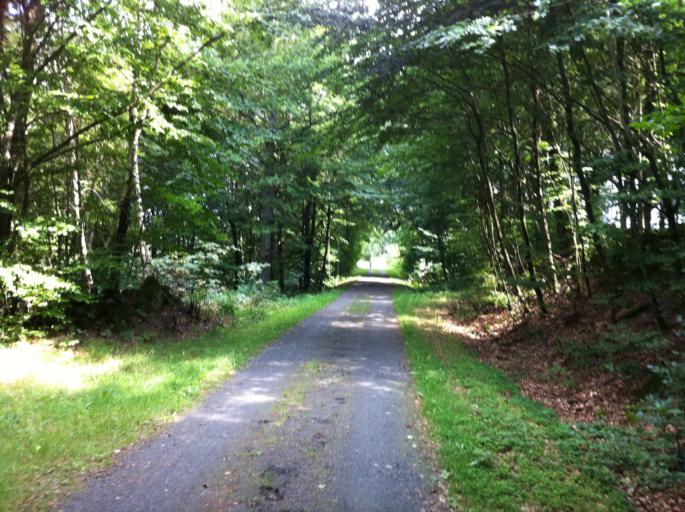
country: SE
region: Skane
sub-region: Hassleholms Kommun
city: Vinslov
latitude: 55.9452
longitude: 13.8521
